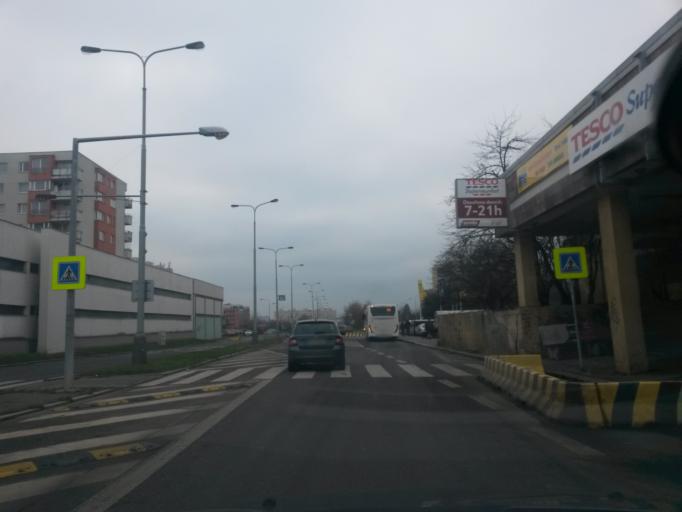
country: CZ
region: Central Bohemia
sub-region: Okres Praha-Zapad
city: Pruhonice
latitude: 50.0320
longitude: 14.5145
